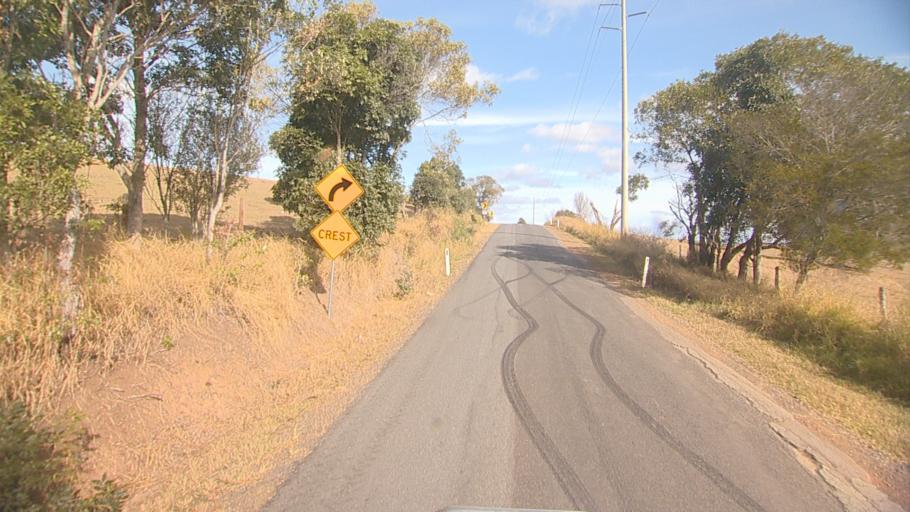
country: AU
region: Queensland
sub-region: Logan
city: Cedar Vale
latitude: -27.9036
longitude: 153.0147
